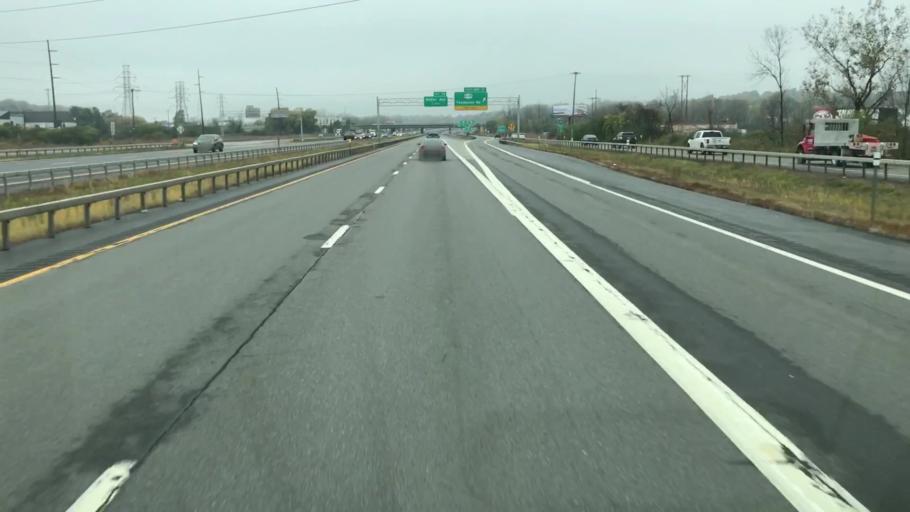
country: US
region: New York
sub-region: Onondaga County
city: East Syracuse
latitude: 43.0579
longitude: -76.0751
